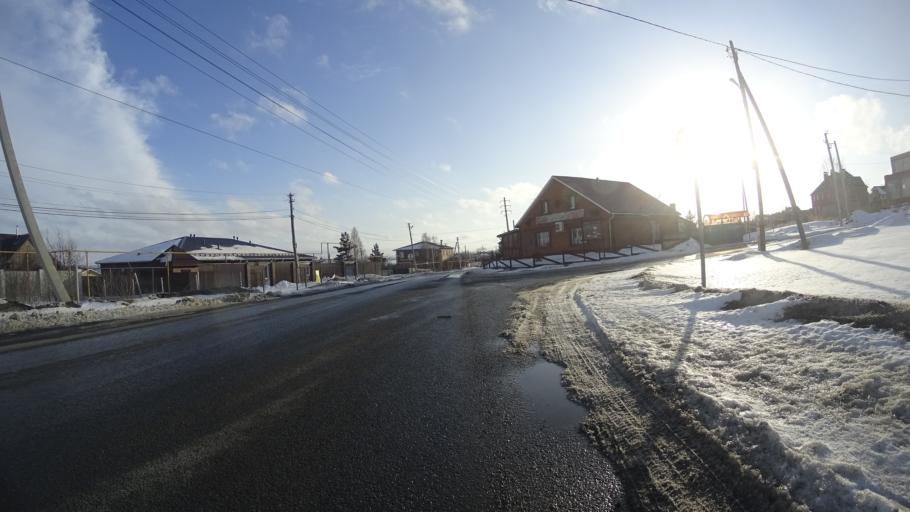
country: RU
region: Chelyabinsk
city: Sargazy
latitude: 55.1150
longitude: 61.2828
